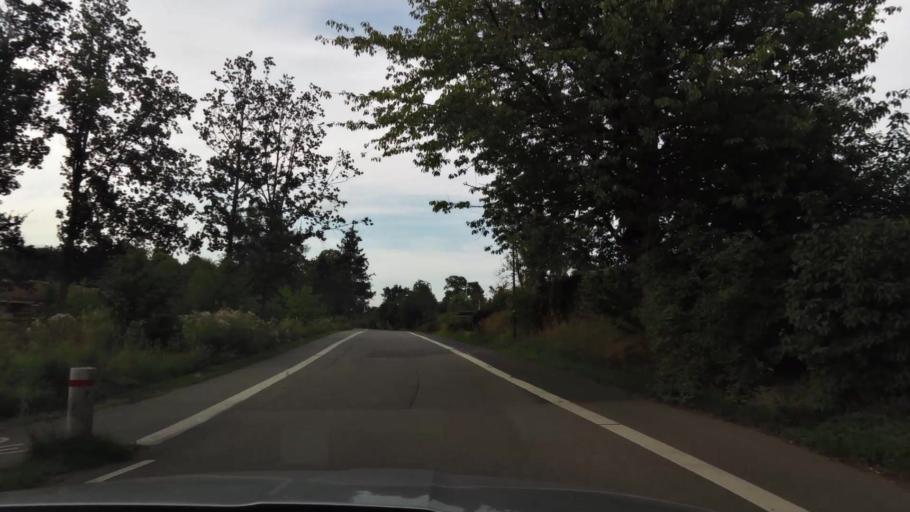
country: DK
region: Capital Region
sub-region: Rudersdal Kommune
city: Birkerod
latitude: 55.8402
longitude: 12.4156
